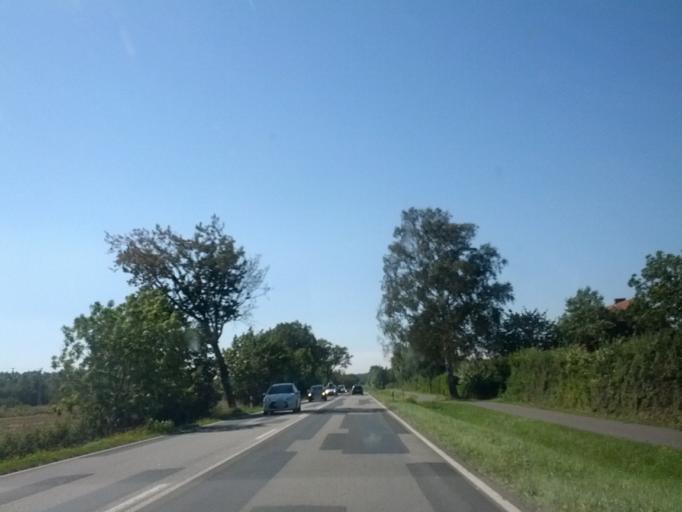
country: DE
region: Mecklenburg-Vorpommern
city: Sagard
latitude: 54.5062
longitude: 13.5319
